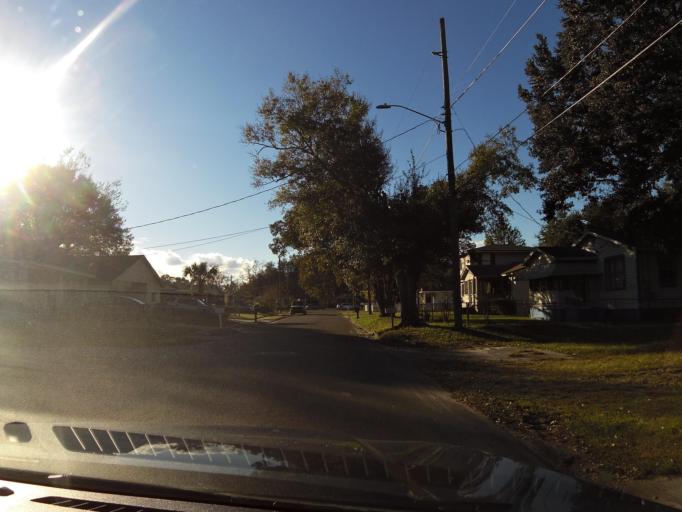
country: US
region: Florida
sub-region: Duval County
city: Jacksonville
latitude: 30.3404
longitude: -81.7002
